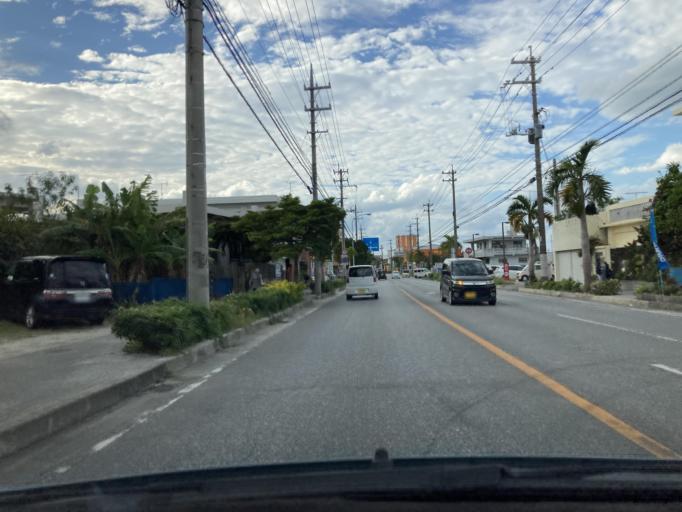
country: JP
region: Okinawa
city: Okinawa
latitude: 26.3588
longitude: 127.8241
